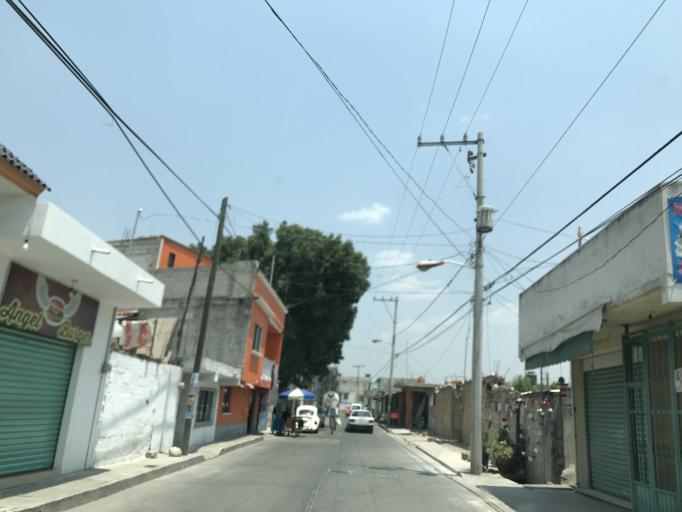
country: MX
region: Tlaxcala
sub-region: Ixtacuixtla de Mariano Matamoros
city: Villa Mariano Matamoros
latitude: 19.3115
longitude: -98.3723
